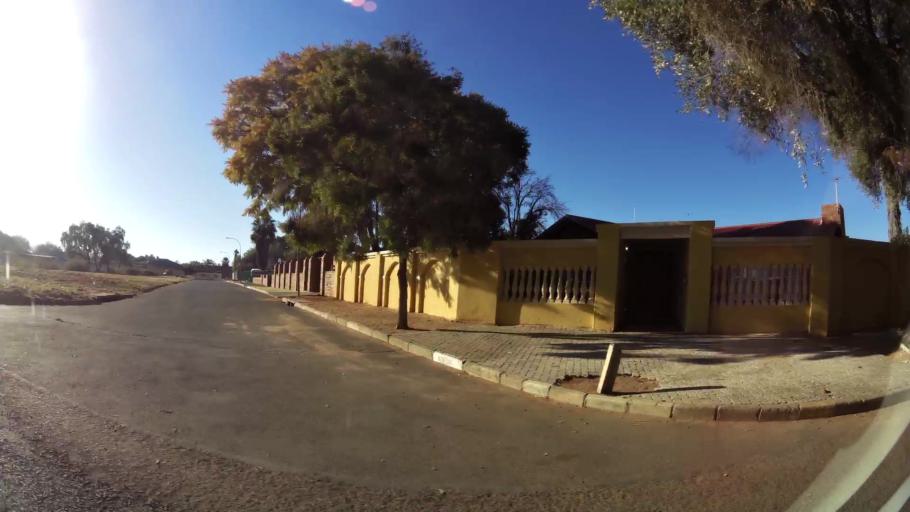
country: ZA
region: Northern Cape
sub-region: Frances Baard District Municipality
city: Kimberley
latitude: -28.7387
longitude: 24.7369
